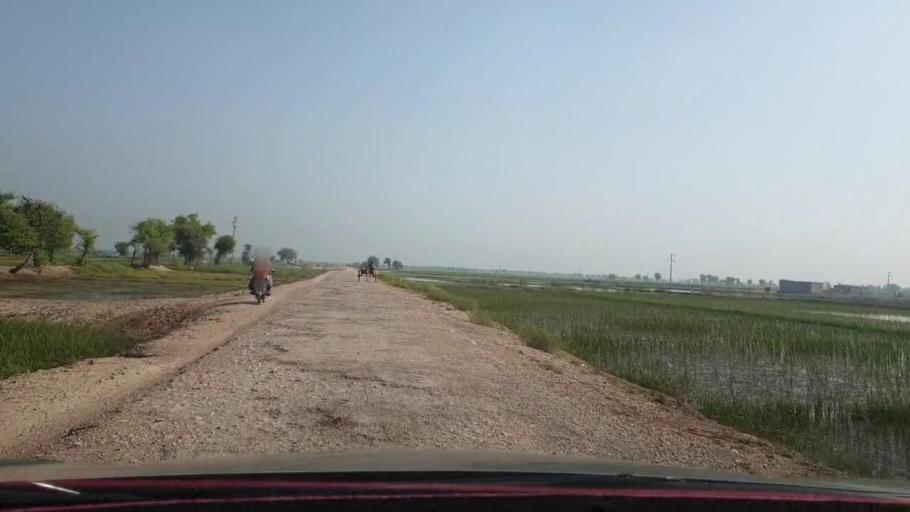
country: PK
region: Sindh
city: Nasirabad
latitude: 27.4941
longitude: 67.9293
